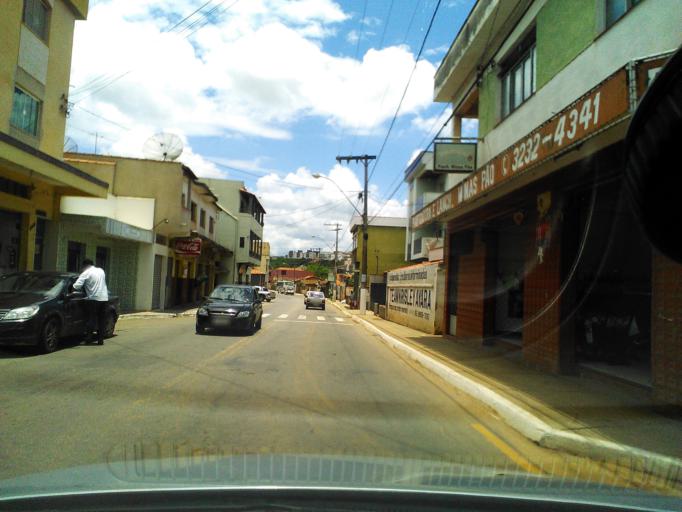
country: BR
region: Minas Gerais
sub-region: Tres Coracoes
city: Tres Coracoes
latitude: -21.7143
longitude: -45.2629
